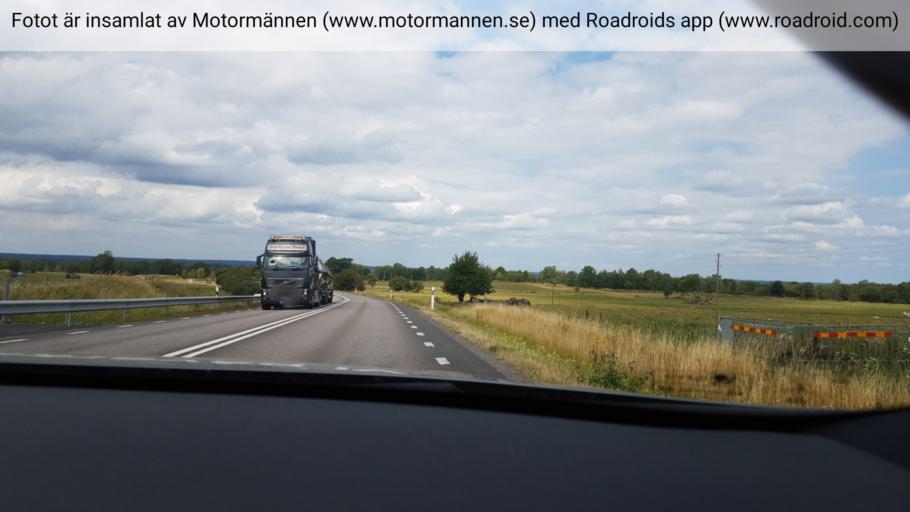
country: SE
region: Vaestra Goetaland
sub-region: Falkopings Kommun
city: Falkoeping
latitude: 58.2373
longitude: 13.5458
